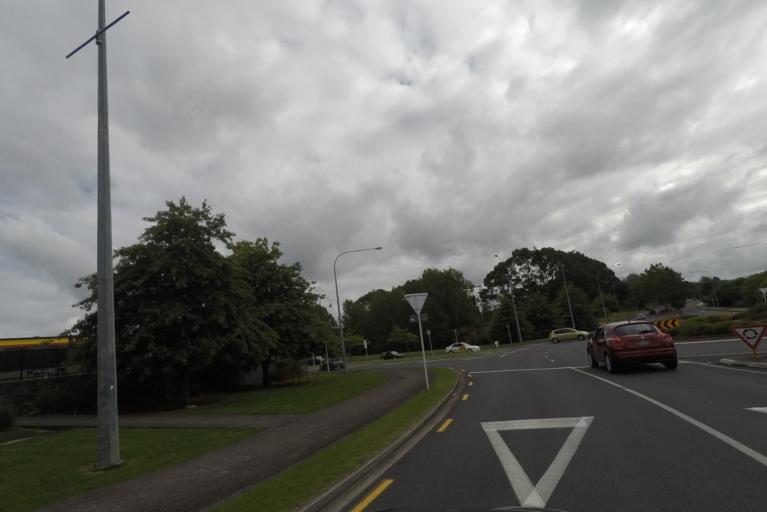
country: NZ
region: Auckland
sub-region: Auckland
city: Rothesay Bay
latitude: -36.7228
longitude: 174.7041
